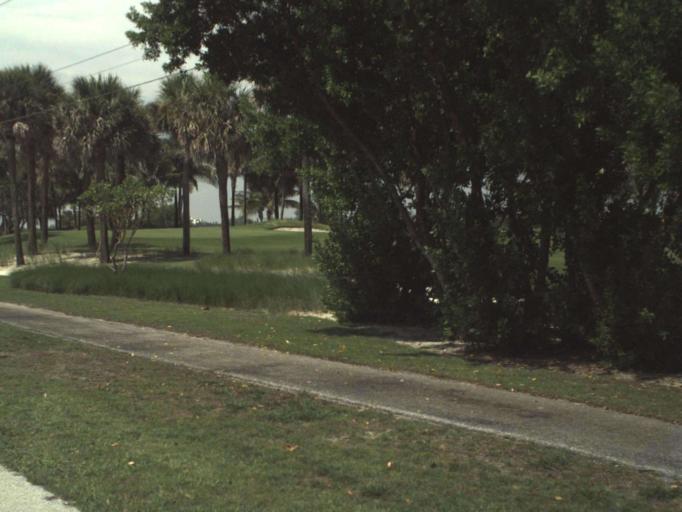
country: US
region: Florida
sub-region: Palm Beach County
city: Lake Worth
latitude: 26.6343
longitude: -80.0392
